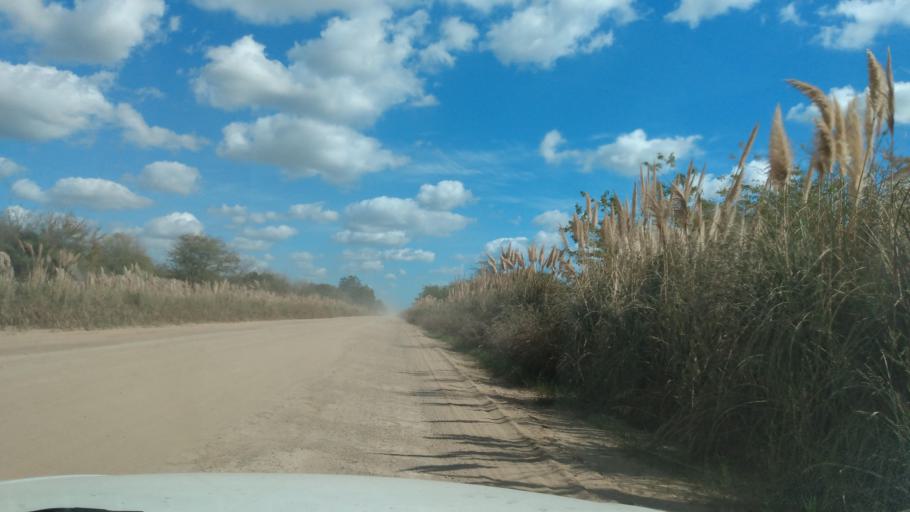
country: AR
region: Buenos Aires
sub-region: Partido de Navarro
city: Navarro
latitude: -34.9990
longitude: -59.3312
